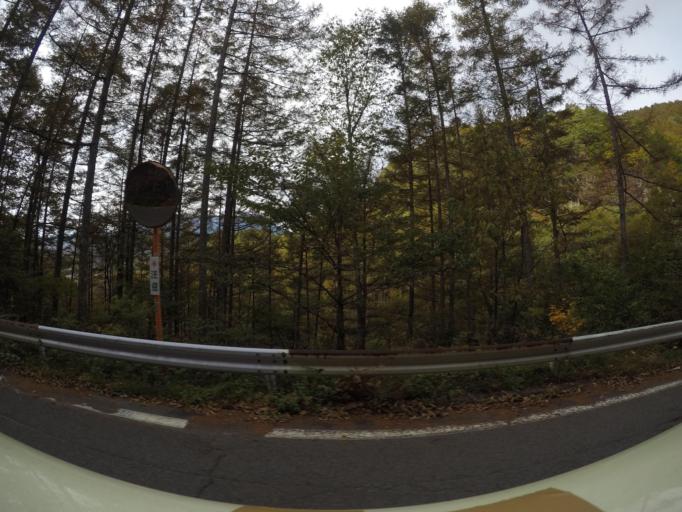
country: JP
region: Nagano
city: Ina
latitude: 35.9383
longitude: 137.5867
